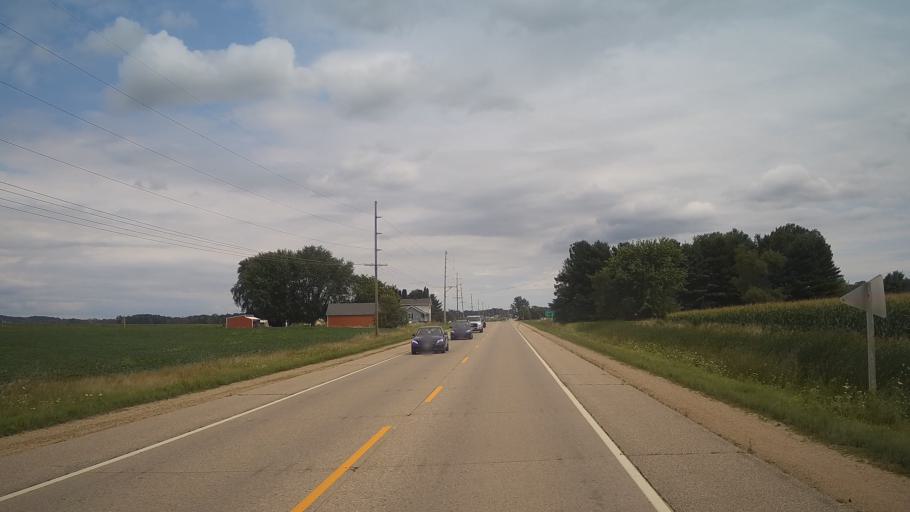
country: US
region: Wisconsin
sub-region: Waushara County
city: Redgranite
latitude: 44.0413
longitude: -89.0356
